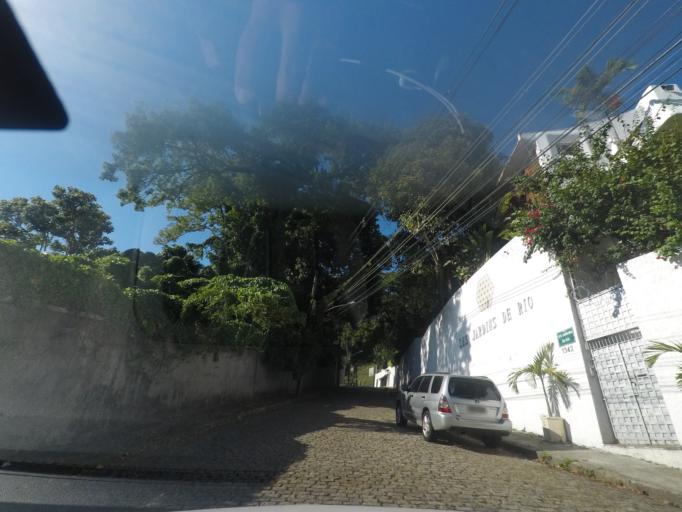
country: BR
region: Rio de Janeiro
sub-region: Rio De Janeiro
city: Rio de Janeiro
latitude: -22.9409
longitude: -43.2060
